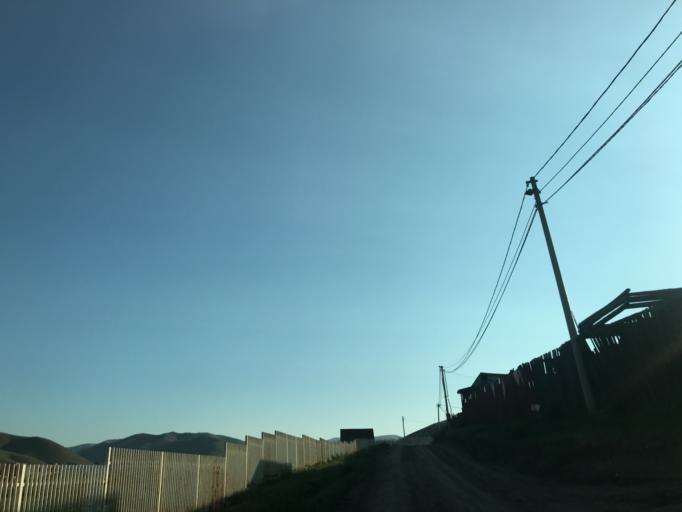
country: MN
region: Ulaanbaatar
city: Ulaanbaatar
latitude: 47.9920
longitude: 106.9666
